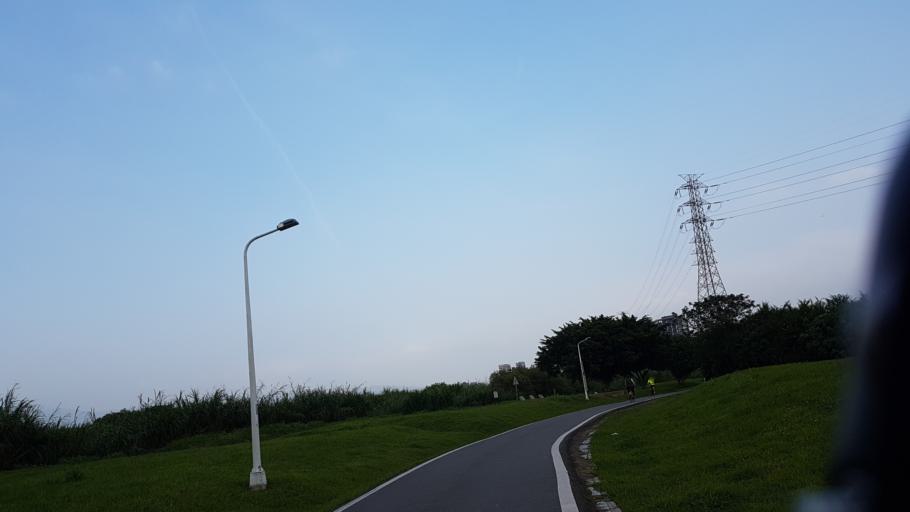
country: TW
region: Taipei
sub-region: Taipei
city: Banqiao
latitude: 25.0364
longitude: 121.4874
